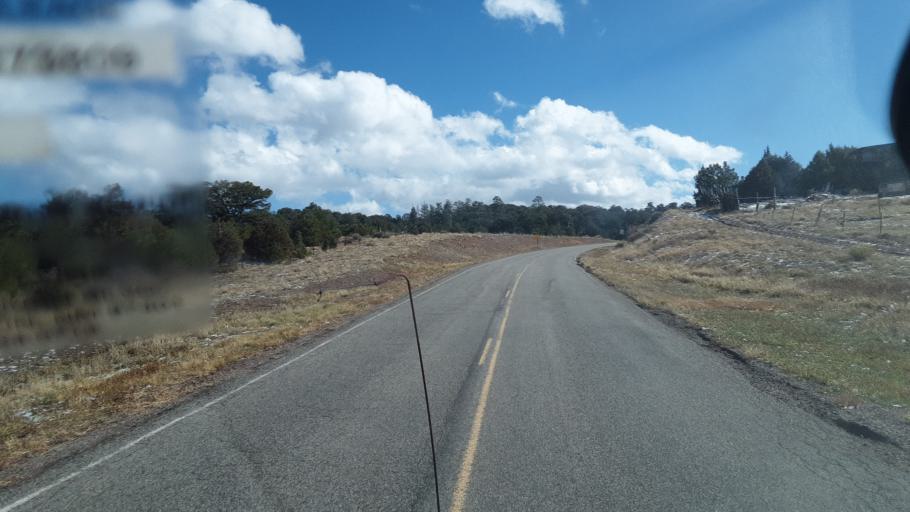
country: US
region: New Mexico
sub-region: Rio Arriba County
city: Santa Teresa
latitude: 36.2320
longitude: -106.8331
